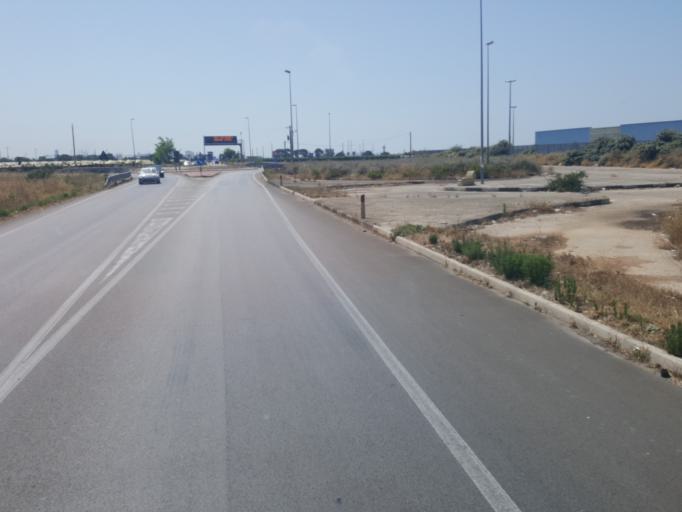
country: IT
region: Apulia
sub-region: Provincia di Taranto
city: Statte
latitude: 40.5361
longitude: 17.1600
